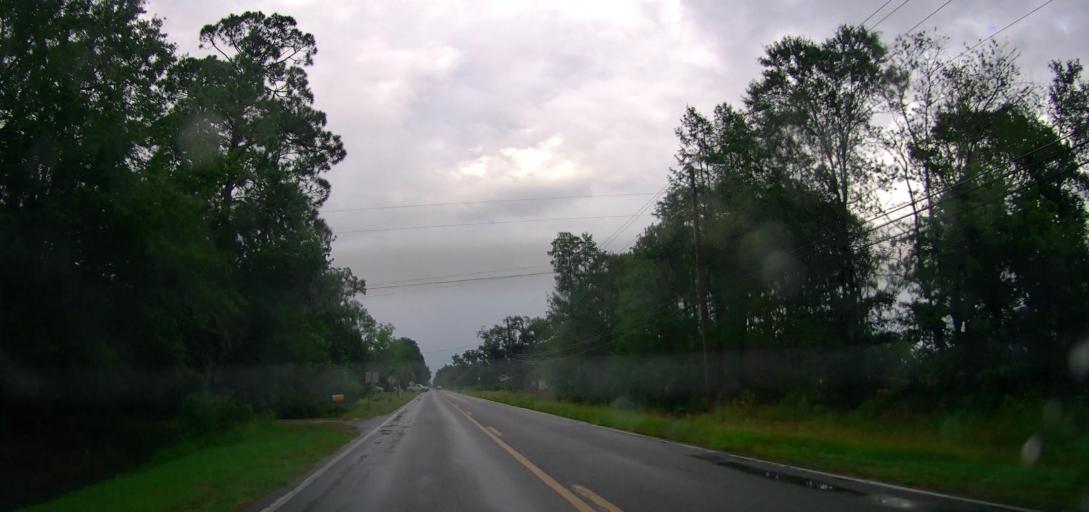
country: US
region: Georgia
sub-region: Ware County
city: Deenwood
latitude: 31.2139
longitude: -82.3874
